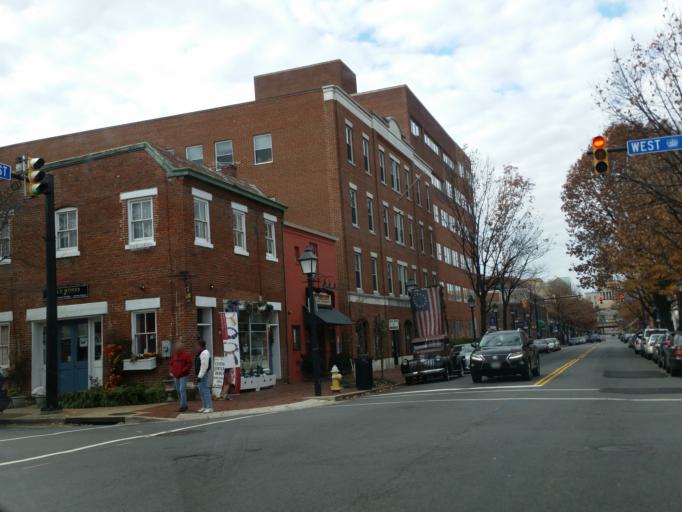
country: US
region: Virginia
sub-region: City of Alexandria
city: Alexandria
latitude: 38.8060
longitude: -77.0545
